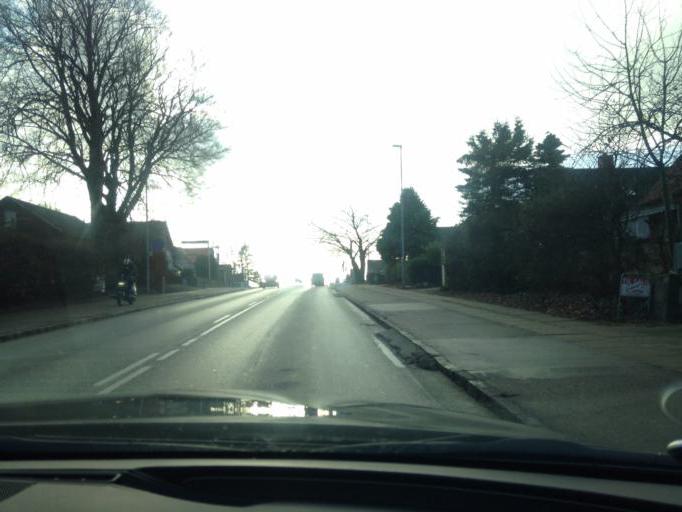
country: DK
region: South Denmark
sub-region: Kolding Kommune
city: Kolding
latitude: 55.5219
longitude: 9.4618
